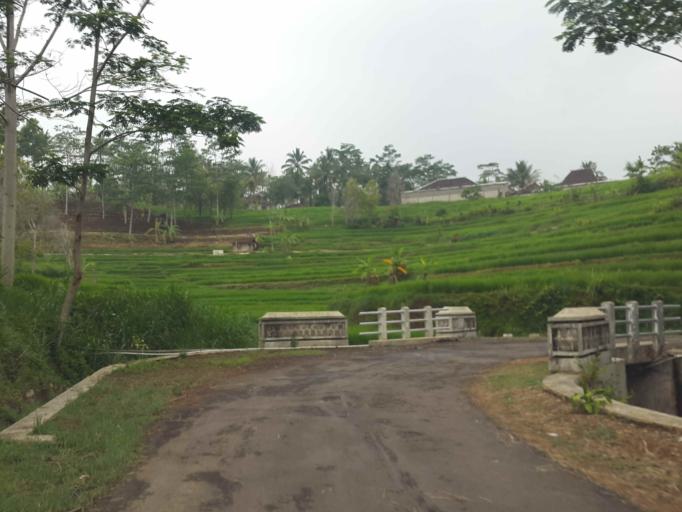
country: ID
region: Central Java
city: Jatiroto
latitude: -7.7080
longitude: 111.0764
